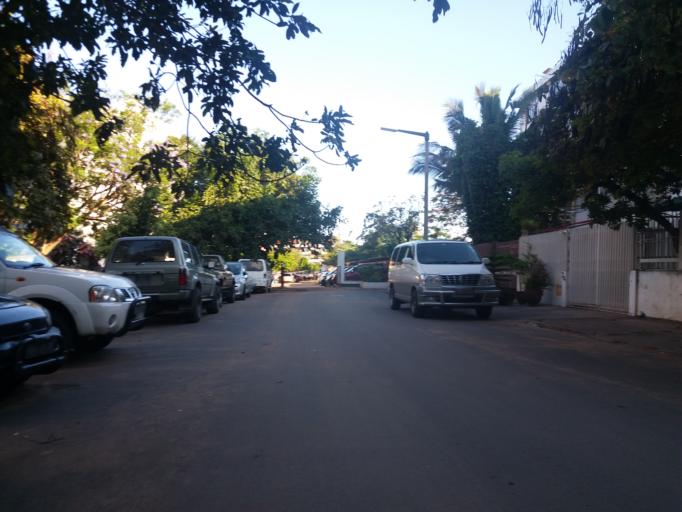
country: MZ
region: Maputo City
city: Maputo
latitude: -25.9508
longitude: 32.5915
